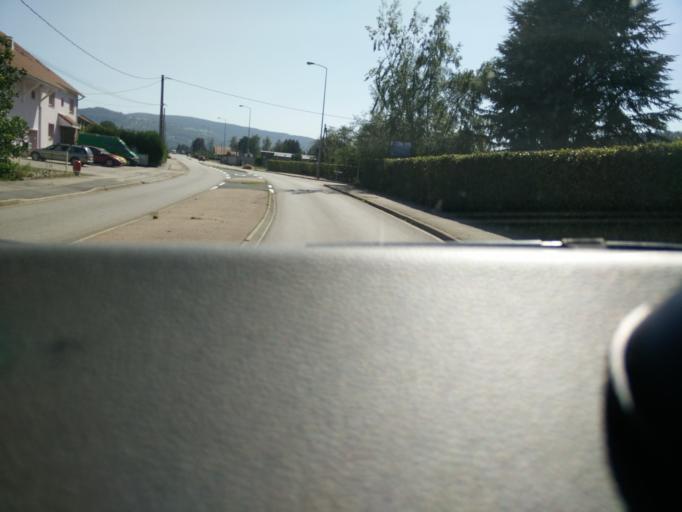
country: FR
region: Lorraine
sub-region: Departement des Vosges
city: Saint-Leonard
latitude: 48.2138
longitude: 6.9420
